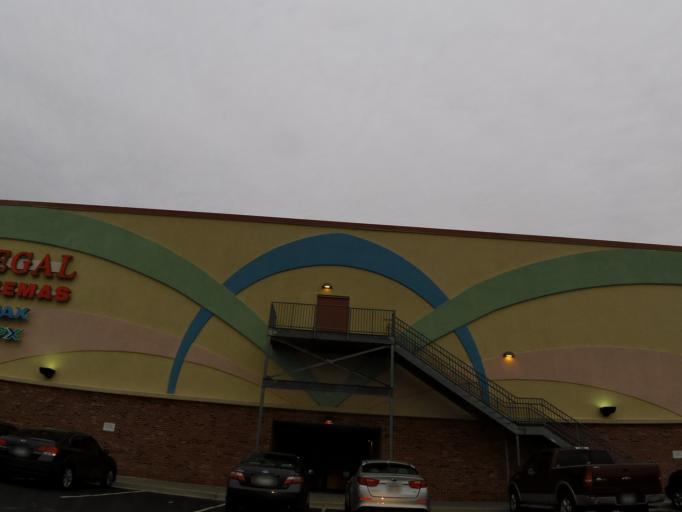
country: US
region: Tennessee
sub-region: Knox County
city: Farragut
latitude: 35.8996
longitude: -84.1568
